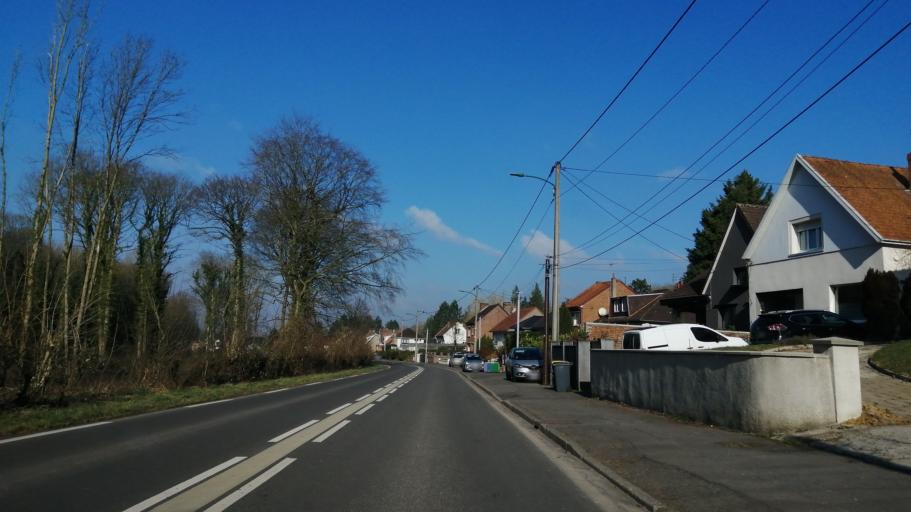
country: FR
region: Nord-Pas-de-Calais
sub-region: Departement du Pas-de-Calais
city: Ranchicourt
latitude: 50.4430
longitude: 2.5530
